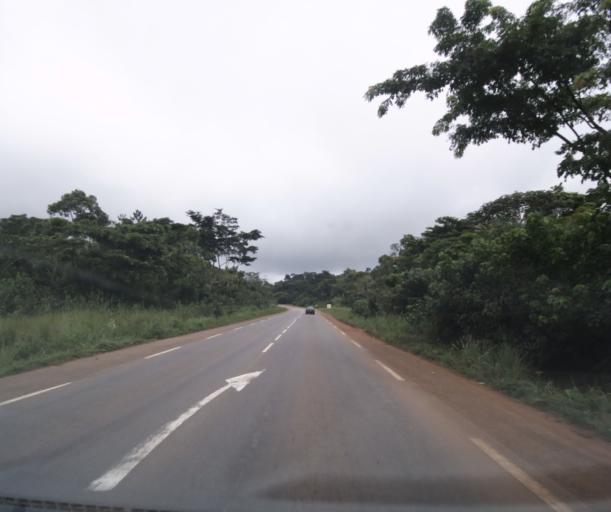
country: CM
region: Centre
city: Mbankomo
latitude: 3.7818
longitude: 11.2718
